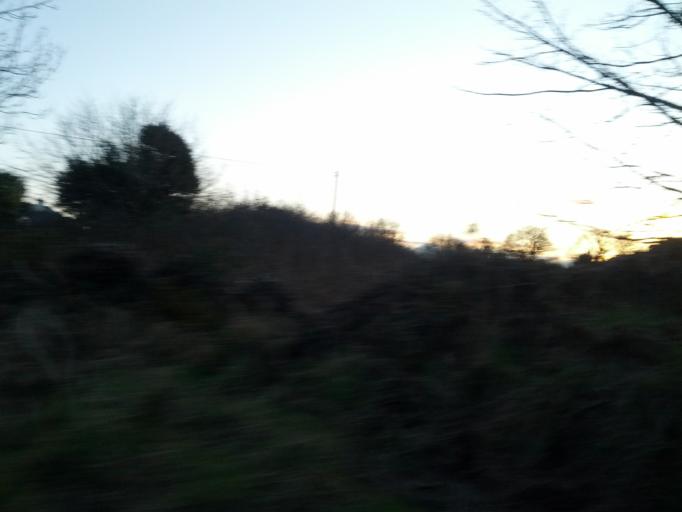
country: IE
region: Connaught
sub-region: County Galway
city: Athenry
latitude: 53.2790
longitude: -8.7582
